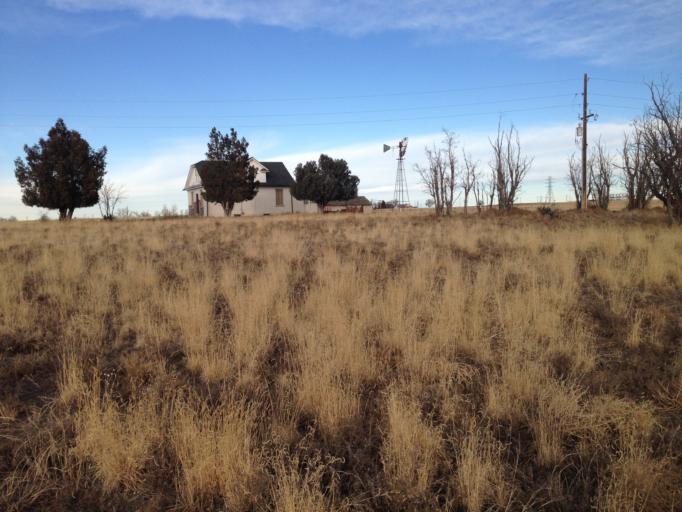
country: US
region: Colorado
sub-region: Adams County
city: Derby
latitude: 39.8213
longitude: -104.8627
